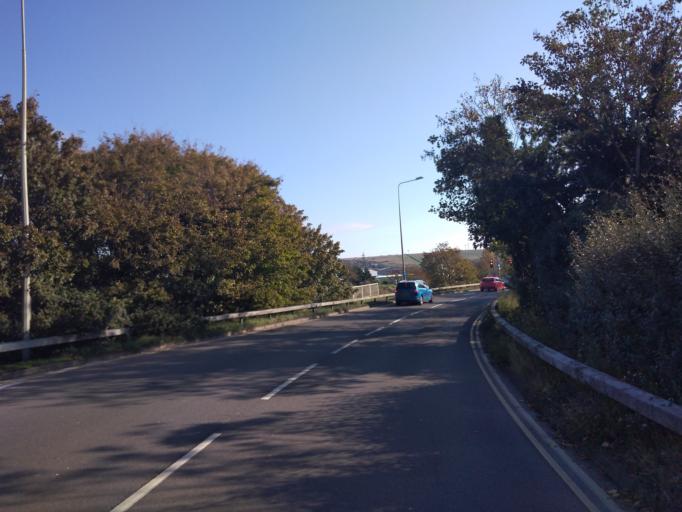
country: GB
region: England
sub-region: East Sussex
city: Newhaven
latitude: 50.7952
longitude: 0.0473
